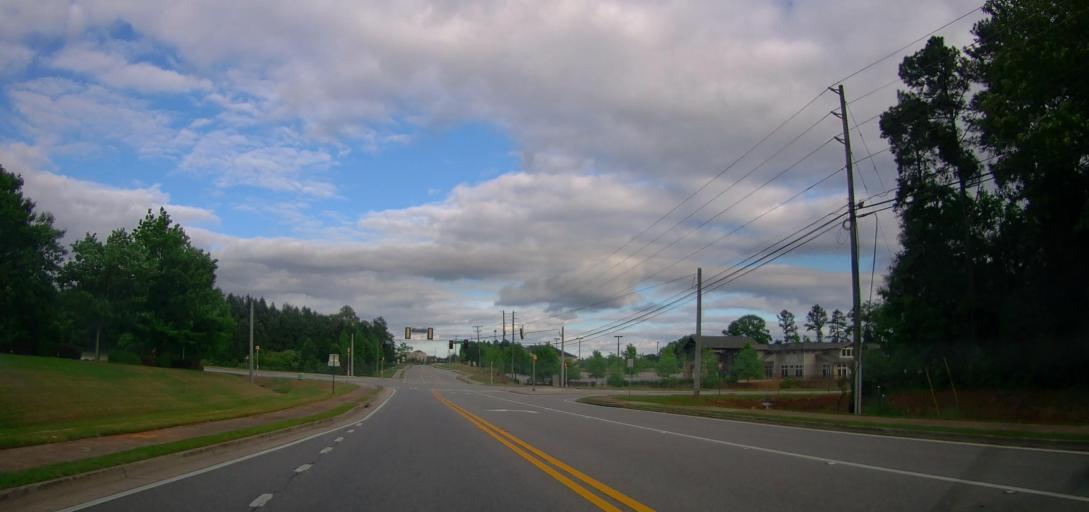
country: US
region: Georgia
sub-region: Oconee County
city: Watkinsville
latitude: 33.9146
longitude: -83.4637
